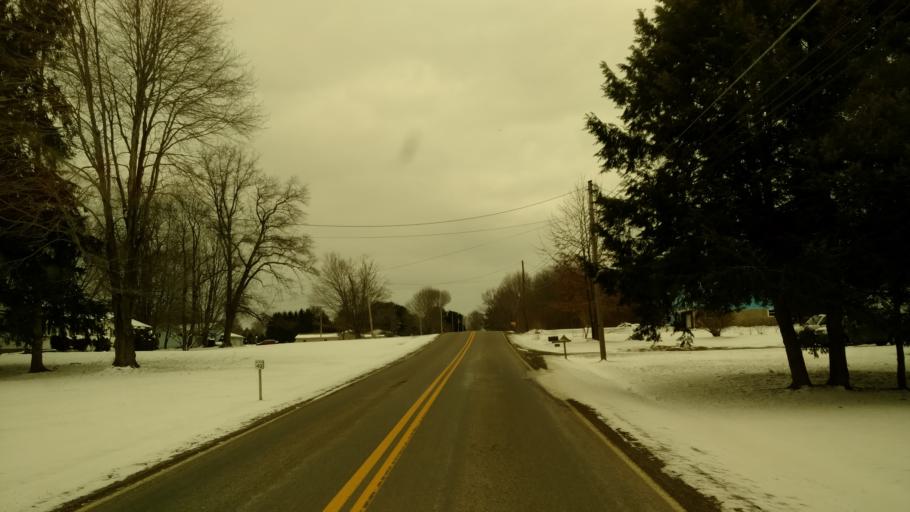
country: US
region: Pennsylvania
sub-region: Mercer County
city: Mercer
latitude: 41.3243
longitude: -80.2367
